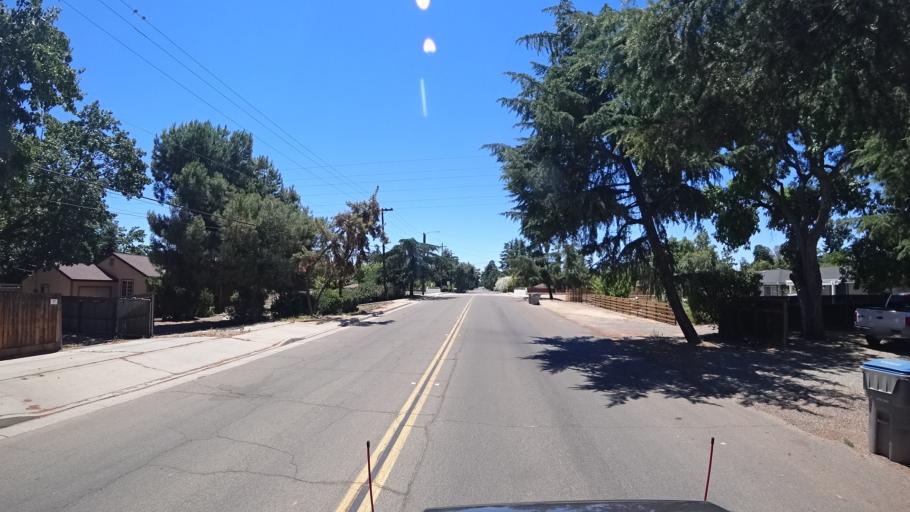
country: US
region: California
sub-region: Fresno County
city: Fresno
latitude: 36.7874
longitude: -119.8024
